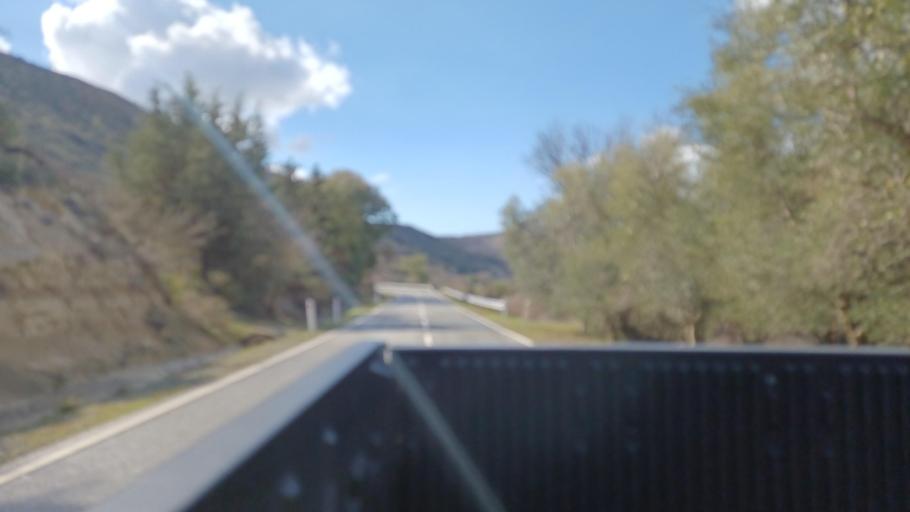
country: CY
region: Limassol
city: Pachna
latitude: 34.7773
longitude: 32.7259
